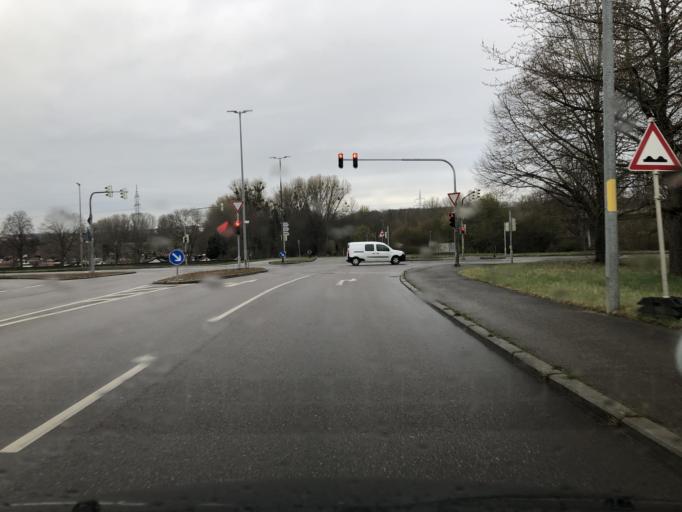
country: DE
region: Baden-Wuerttemberg
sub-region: Regierungsbezirk Stuttgart
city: Magstadt
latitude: 48.7105
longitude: 8.9788
